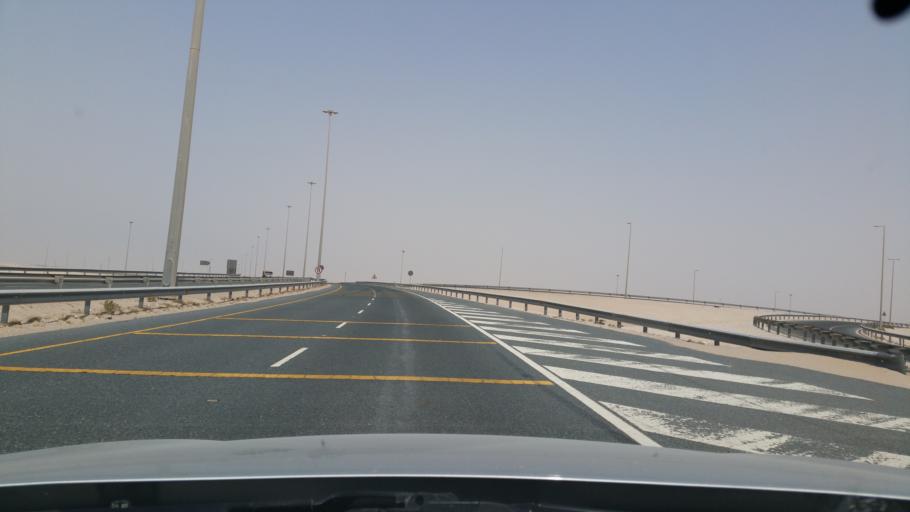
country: QA
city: Umm Bab
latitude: 24.9368
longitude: 50.9938
